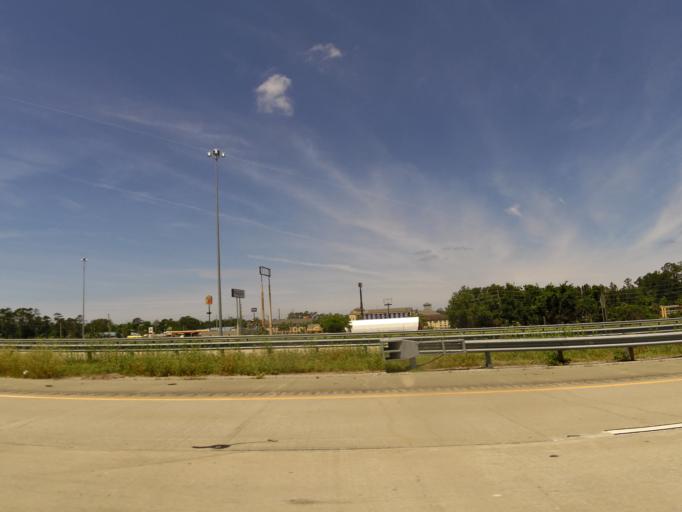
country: US
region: Georgia
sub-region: Glynn County
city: Dock Junction
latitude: 31.2218
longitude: -81.5215
